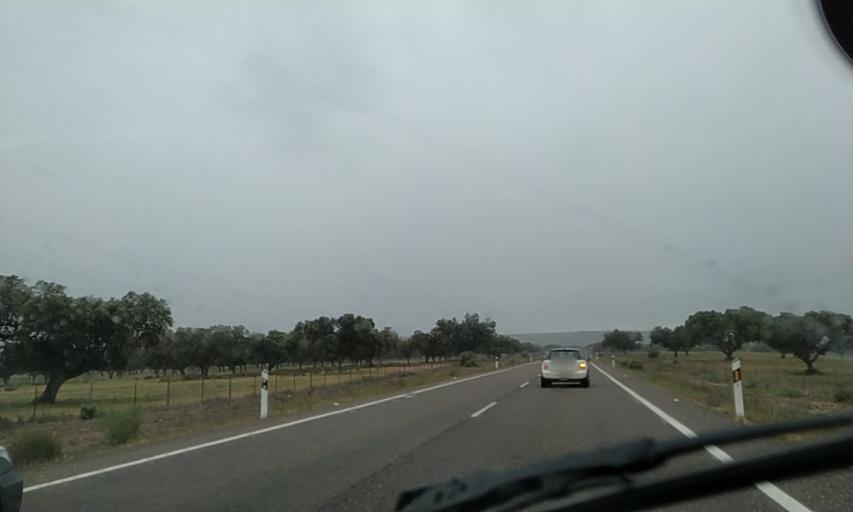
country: ES
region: Extremadura
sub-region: Provincia de Badajoz
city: La Roca de la Sierra
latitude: 39.1041
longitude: -6.7104
